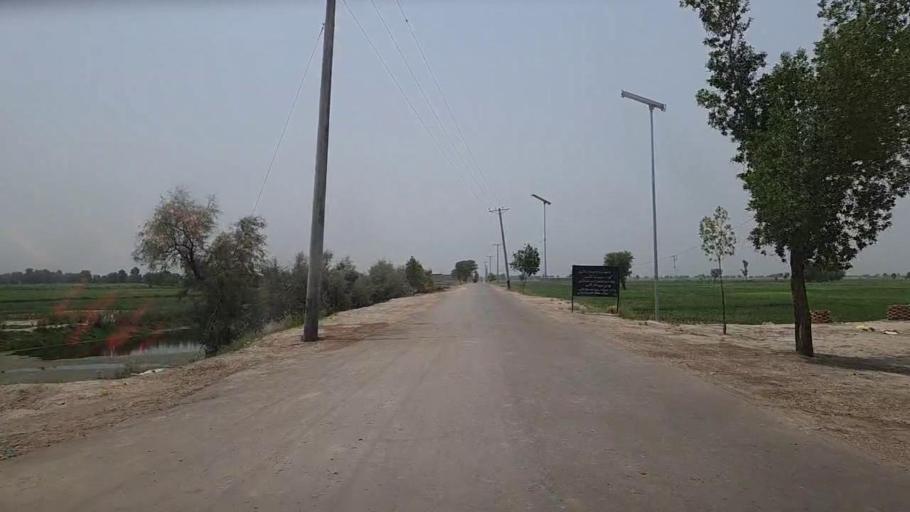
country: PK
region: Sindh
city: Sita Road
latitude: 27.0583
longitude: 67.9035
